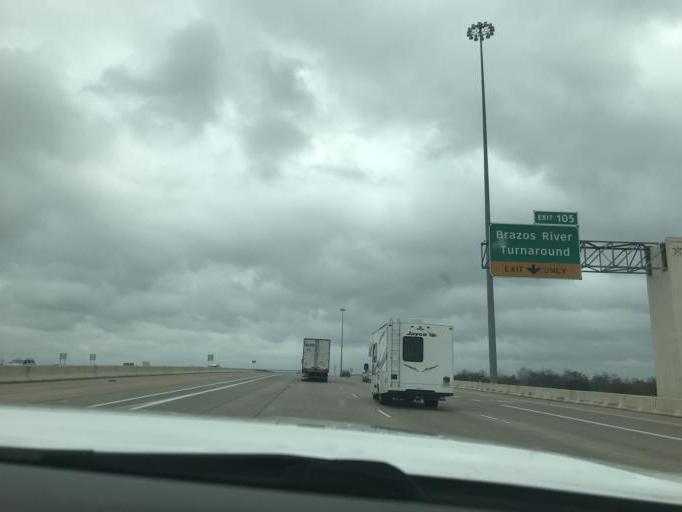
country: US
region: Texas
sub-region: Fort Bend County
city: Greatwood
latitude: 29.5609
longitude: -95.6926
